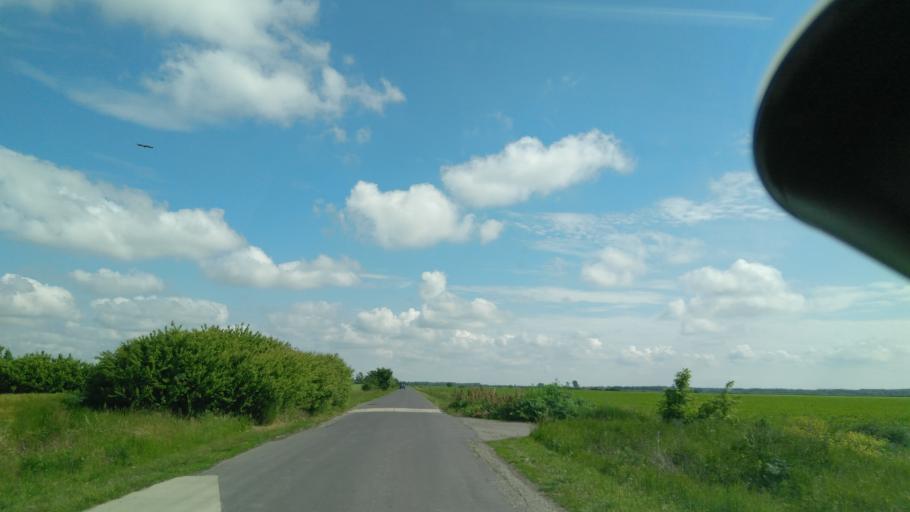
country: HU
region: Bekes
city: Bekes
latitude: 46.8128
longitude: 21.1475
